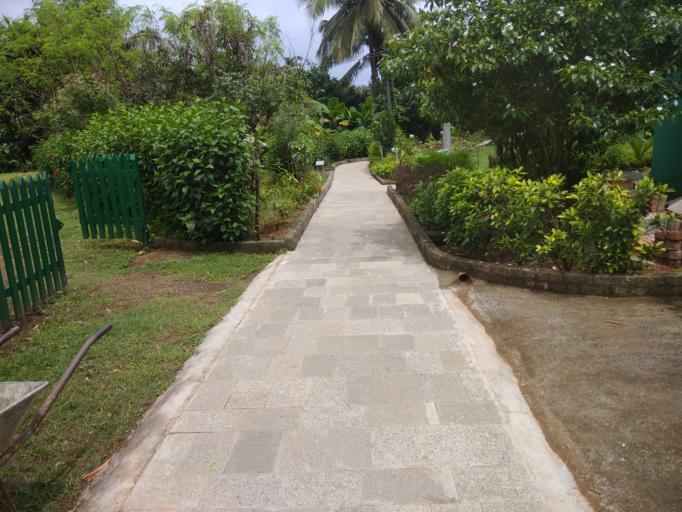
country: IN
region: Kerala
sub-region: Thrissur District
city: Trichur
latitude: 10.4580
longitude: 76.2386
